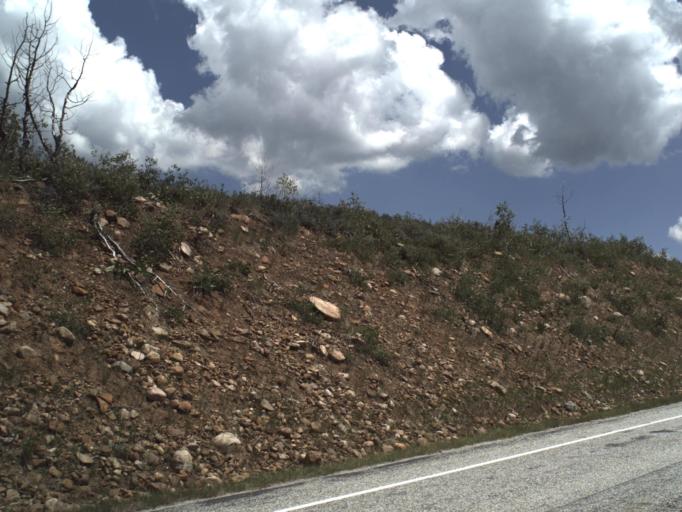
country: US
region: Utah
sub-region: Weber County
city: Wolf Creek
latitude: 41.4093
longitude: -111.5571
